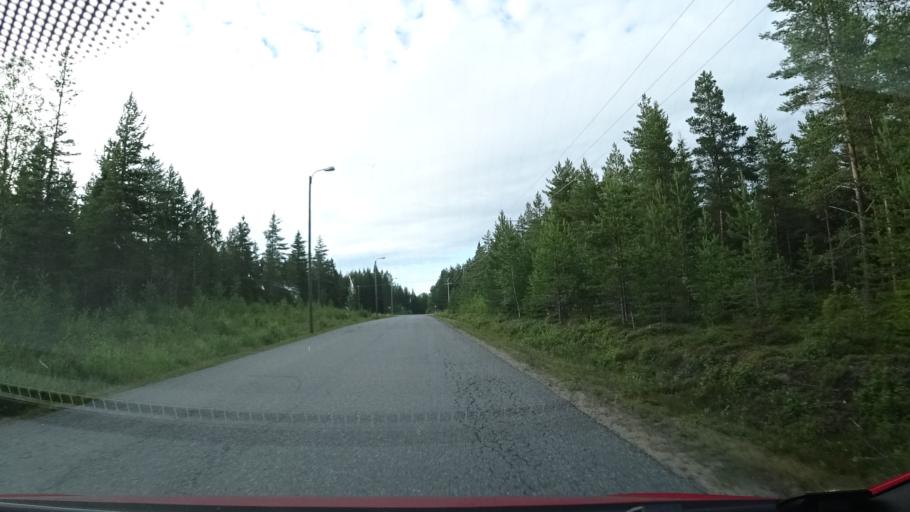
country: FI
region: Northern Ostrobothnia
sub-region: Oulu
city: Haukipudas
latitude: 65.1993
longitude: 25.4134
